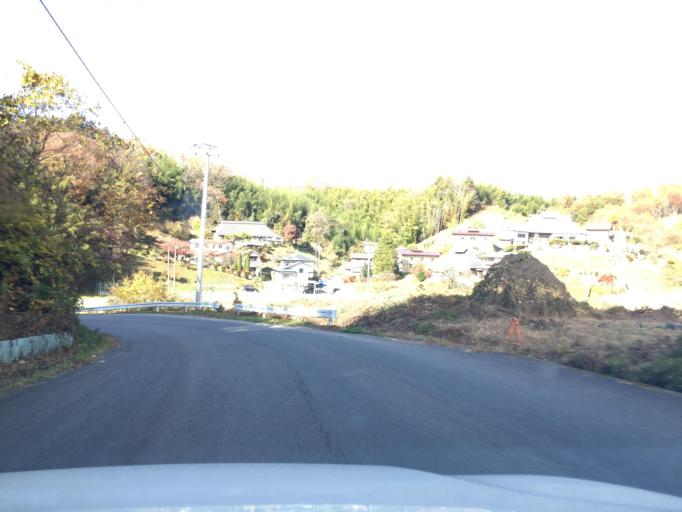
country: JP
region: Fukushima
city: Miharu
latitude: 37.4599
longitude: 140.4995
